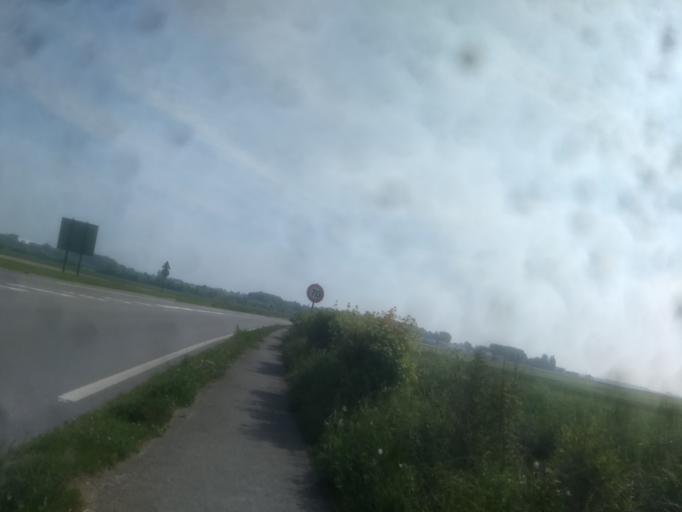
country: FR
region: Nord-Pas-de-Calais
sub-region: Departement du Pas-de-Calais
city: Beaurains
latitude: 50.2696
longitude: 2.8019
